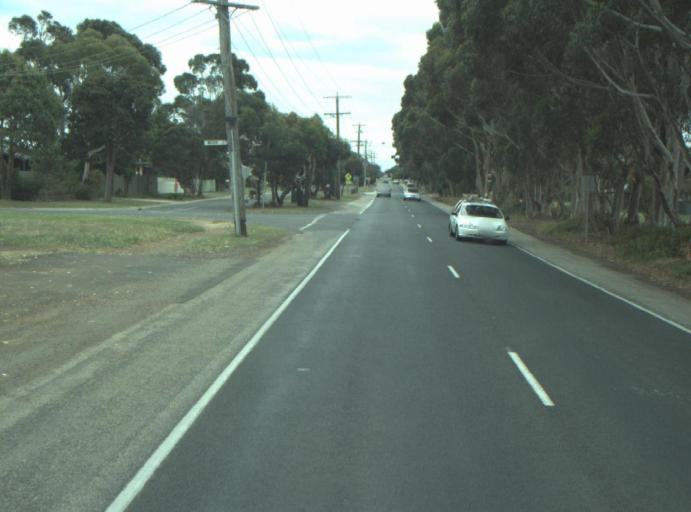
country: AU
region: Victoria
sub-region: Greater Geelong
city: Leopold
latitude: -38.2617
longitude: 144.5347
